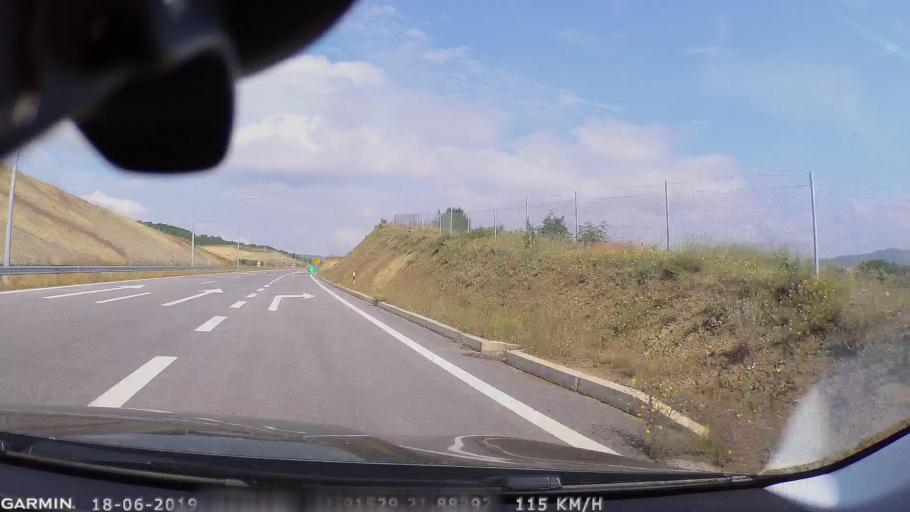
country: MK
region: Sveti Nikole
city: Gorobinci
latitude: 41.9140
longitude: 21.8887
